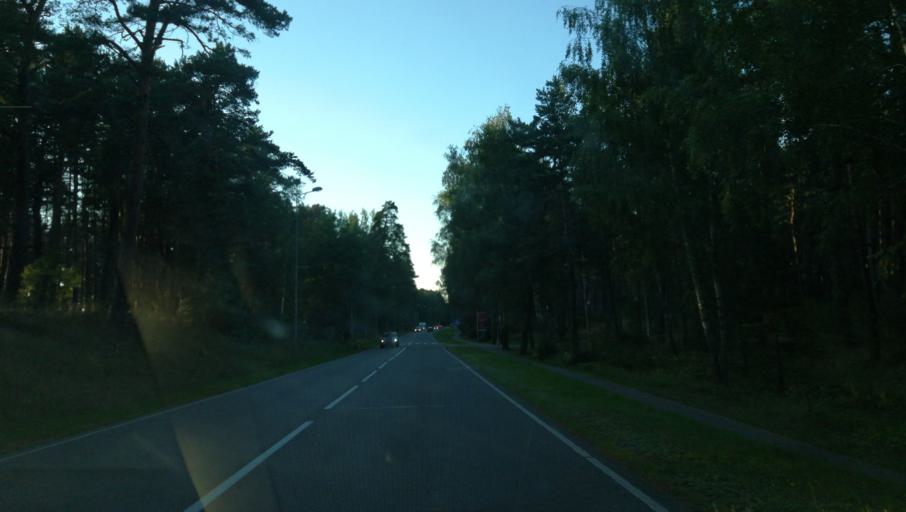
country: LV
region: Saulkrastu
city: Saulkrasti
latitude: 57.2900
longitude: 24.4116
